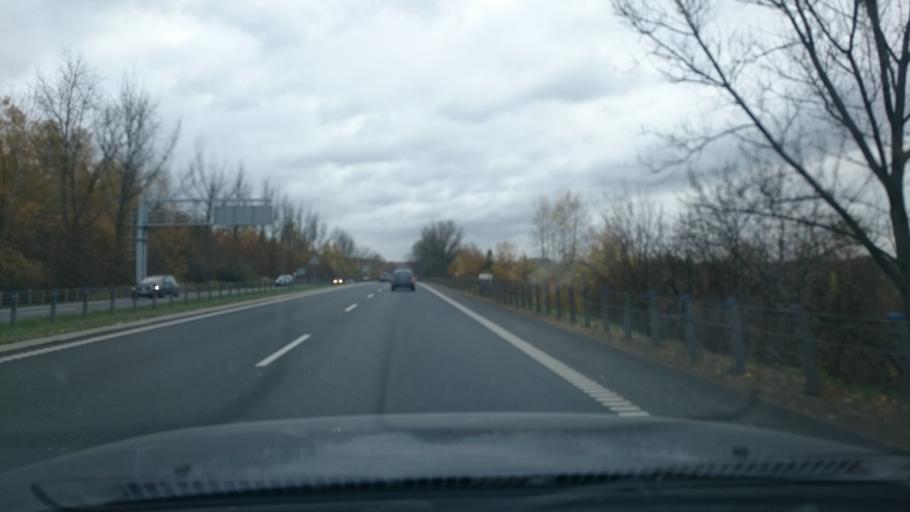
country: PL
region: Silesian Voivodeship
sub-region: Dabrowa Gornicza
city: Dabrowa Gornicza
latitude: 50.3171
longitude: 19.2582
